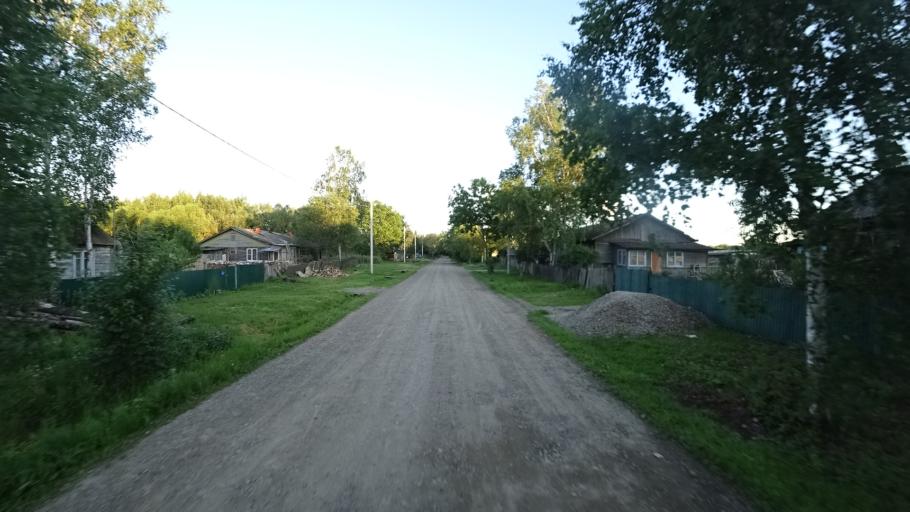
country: RU
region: Khabarovsk Krai
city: Khor
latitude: 47.8517
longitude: 134.9832
